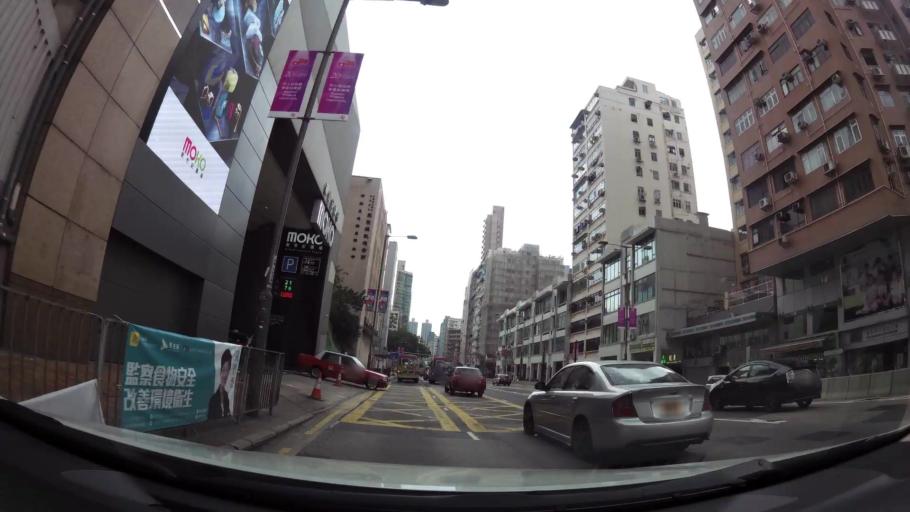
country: HK
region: Kowloon City
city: Kowloon
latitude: 22.3248
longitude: 114.1734
